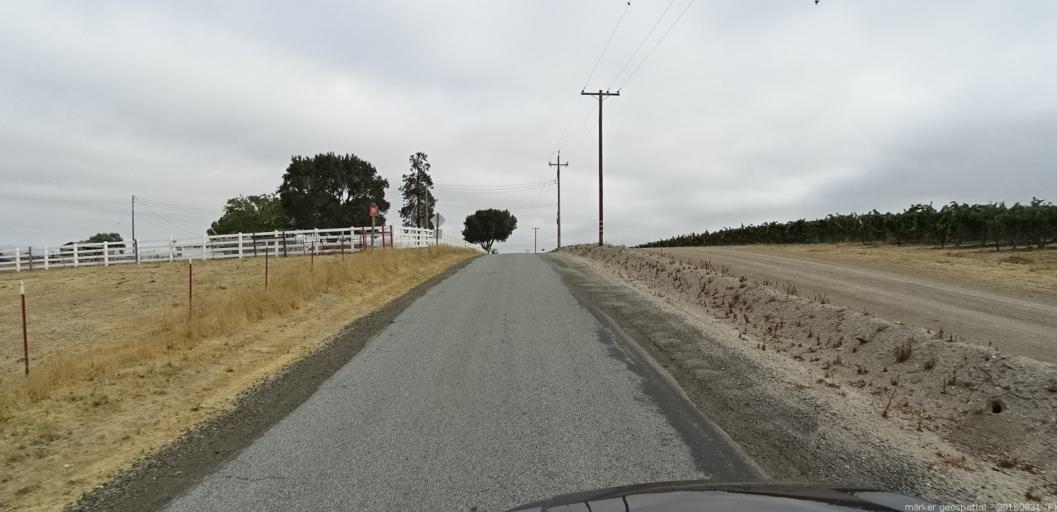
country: US
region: California
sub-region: Monterey County
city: King City
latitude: 36.1407
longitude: -121.1005
